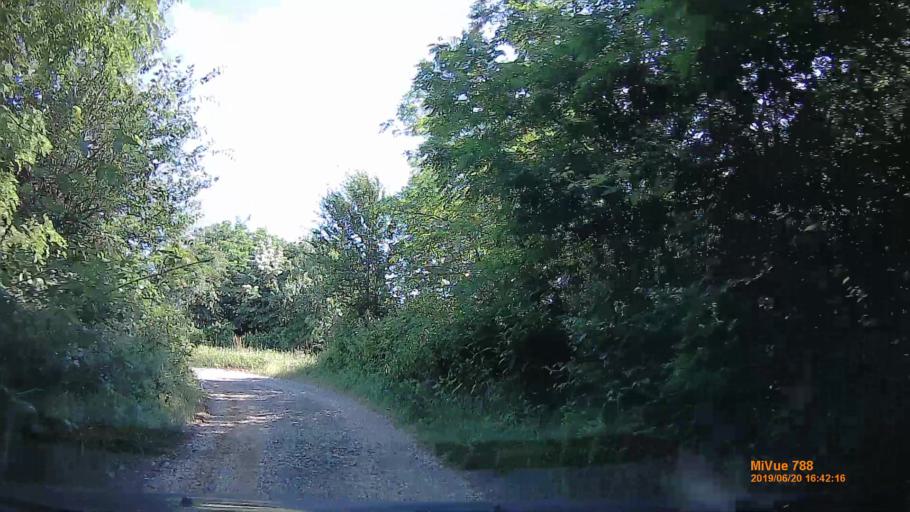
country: HU
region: Baranya
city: Buekkoesd
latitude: 46.1616
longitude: 18.0351
